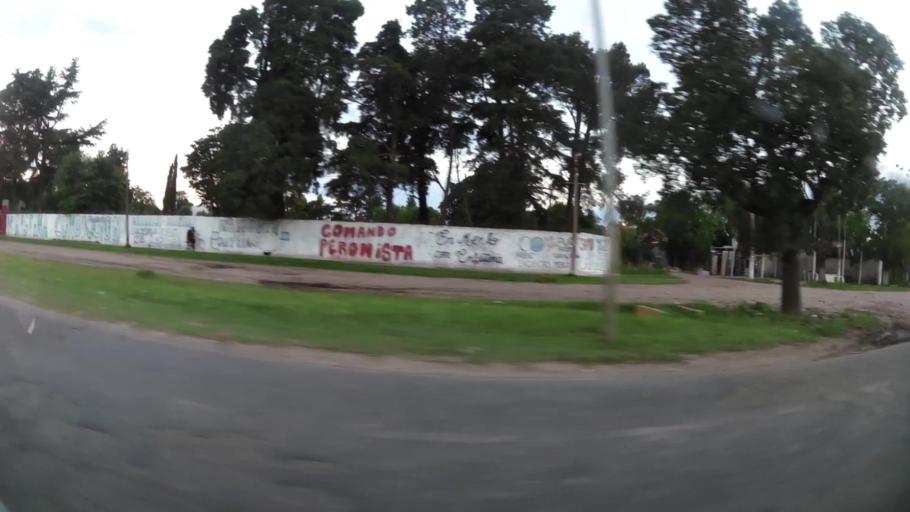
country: AR
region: Buenos Aires
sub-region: Partido de Merlo
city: Merlo
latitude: -34.6870
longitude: -58.7649
